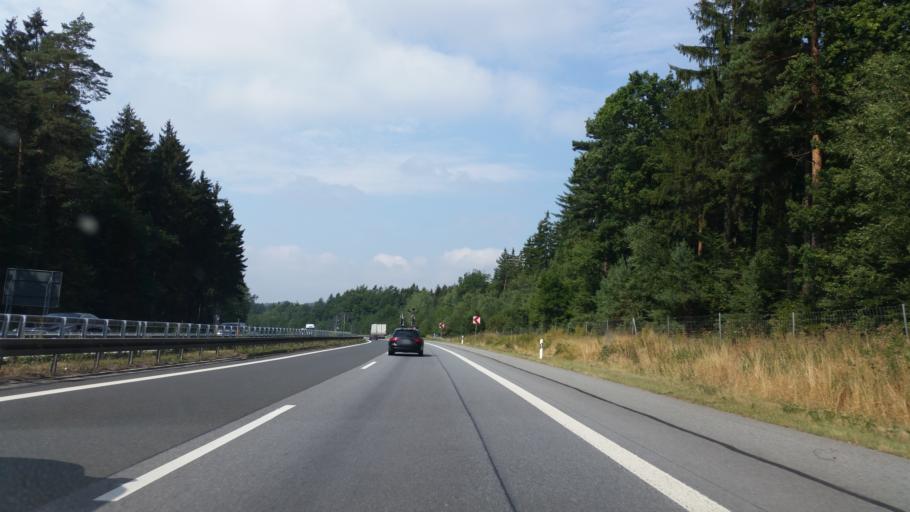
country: DE
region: Saxony
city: Hauswalde
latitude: 51.1755
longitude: 14.1045
